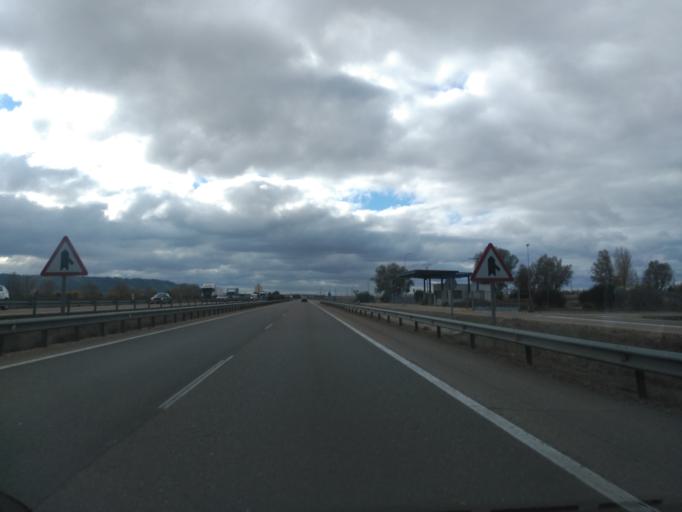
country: ES
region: Castille and Leon
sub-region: Provincia de Valladolid
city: Cabezon
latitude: 41.7760
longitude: -4.6182
